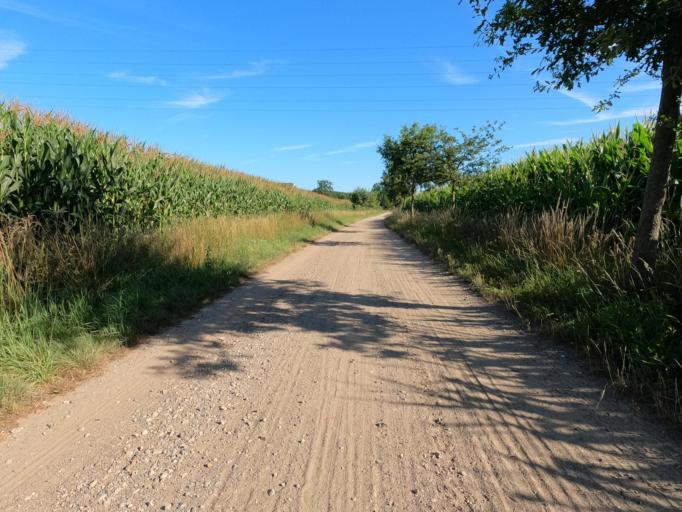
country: BE
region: Flanders
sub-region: Provincie Antwerpen
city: Herenthout
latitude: 51.1525
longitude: 4.7367
